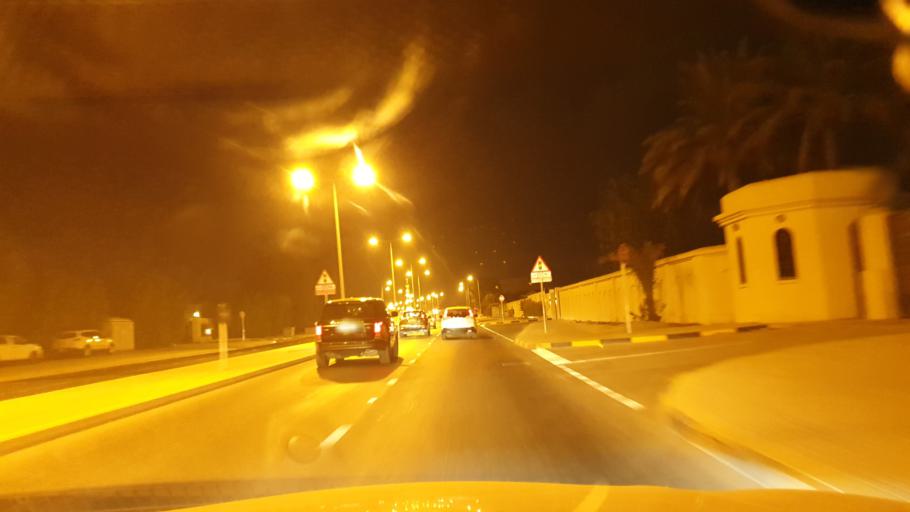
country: BH
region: Manama
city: Jidd Hafs
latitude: 26.2061
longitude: 50.4830
